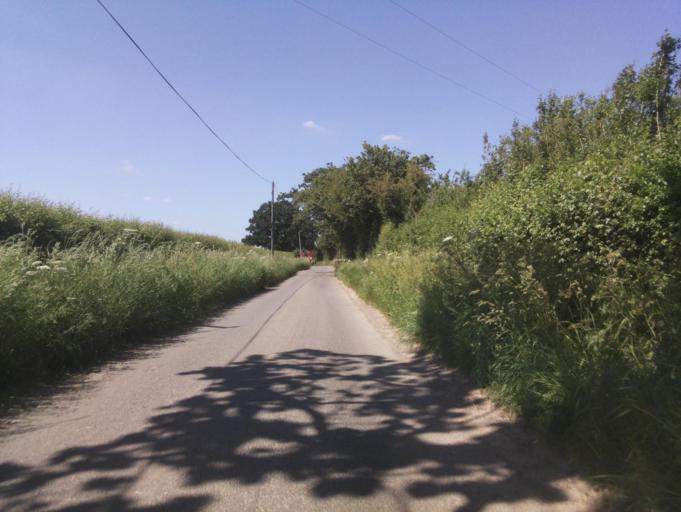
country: GB
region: England
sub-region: Wiltshire
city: Bremhill
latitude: 51.4637
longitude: -2.0704
